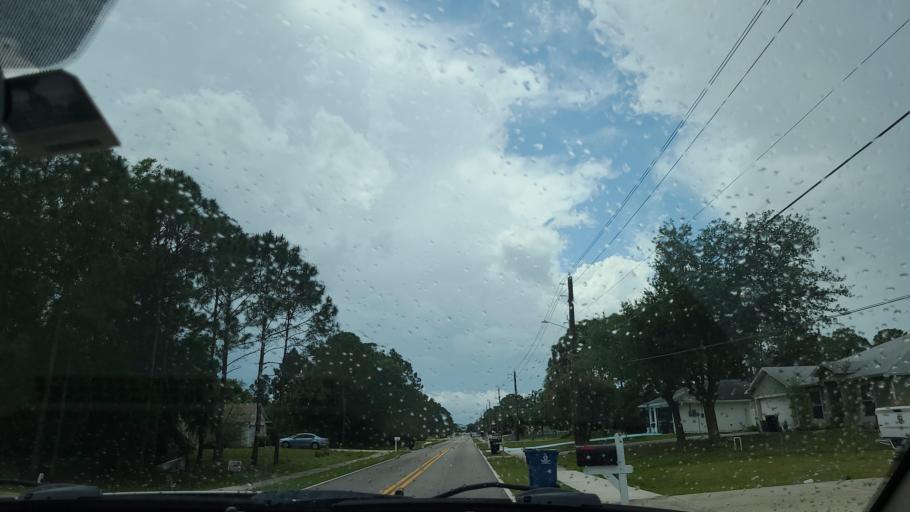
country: US
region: Florida
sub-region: Brevard County
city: Grant-Valkaria
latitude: 27.9491
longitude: -80.6403
